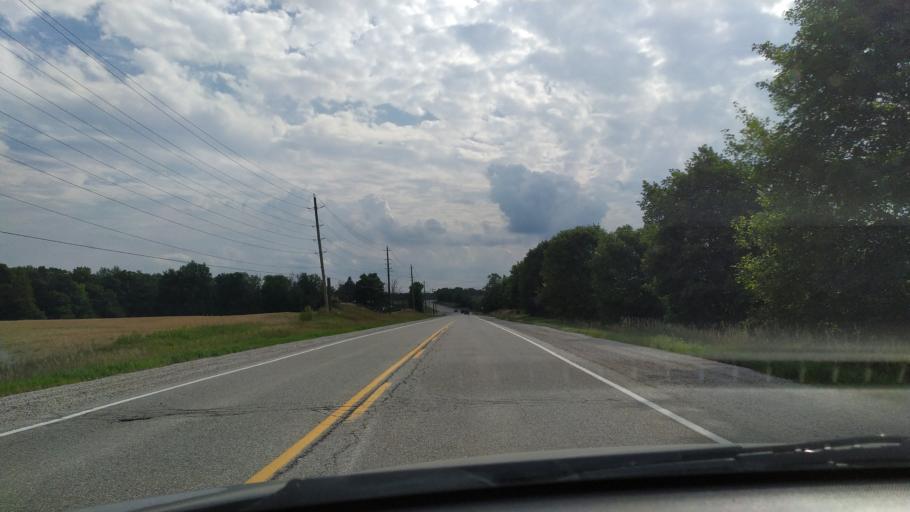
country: CA
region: Ontario
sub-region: Wellington County
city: Guelph
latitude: 43.4632
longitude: -80.1681
